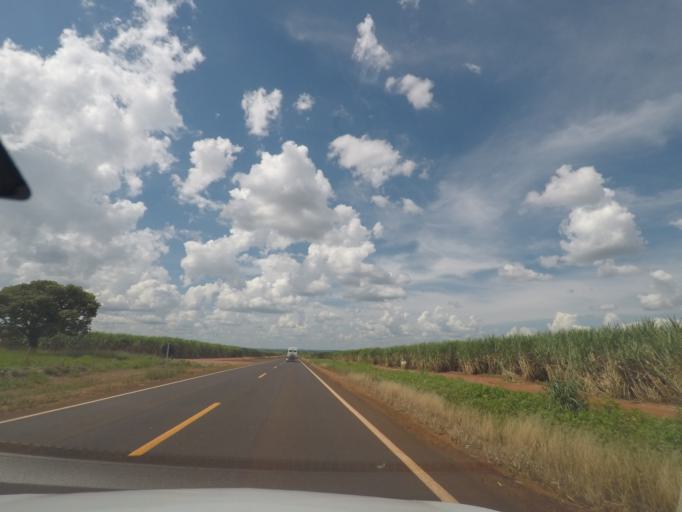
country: BR
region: Minas Gerais
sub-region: Conceicao Das Alagoas
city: Conceicao das Alagoas
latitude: -19.8455
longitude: -48.5949
